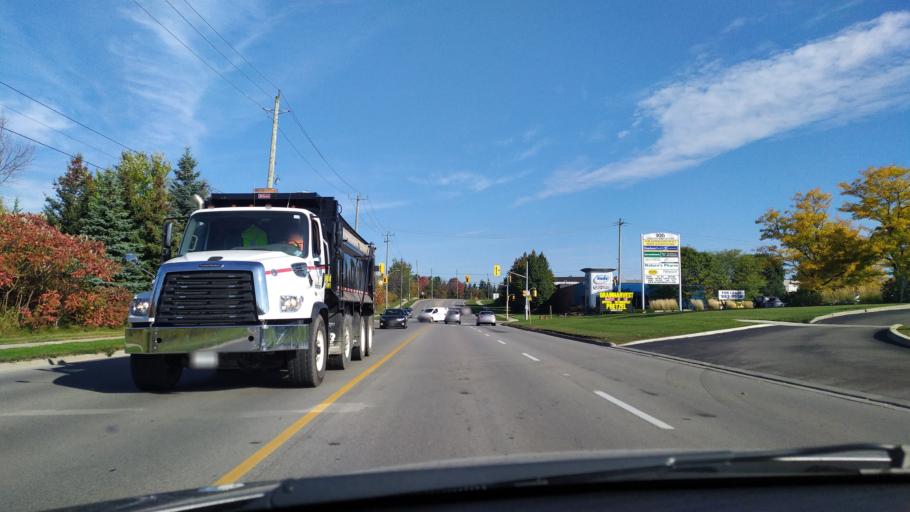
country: CA
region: Ontario
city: Waterloo
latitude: 43.4865
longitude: -80.5183
